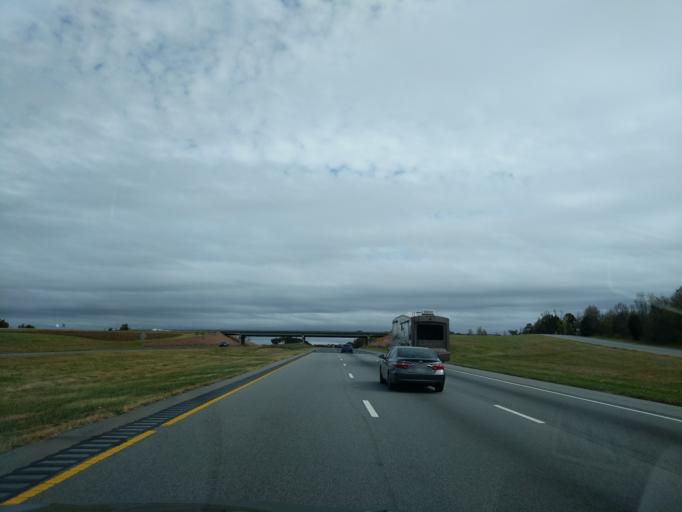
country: US
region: North Carolina
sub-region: Davidson County
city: Tyro
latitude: 35.7732
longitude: -80.3178
